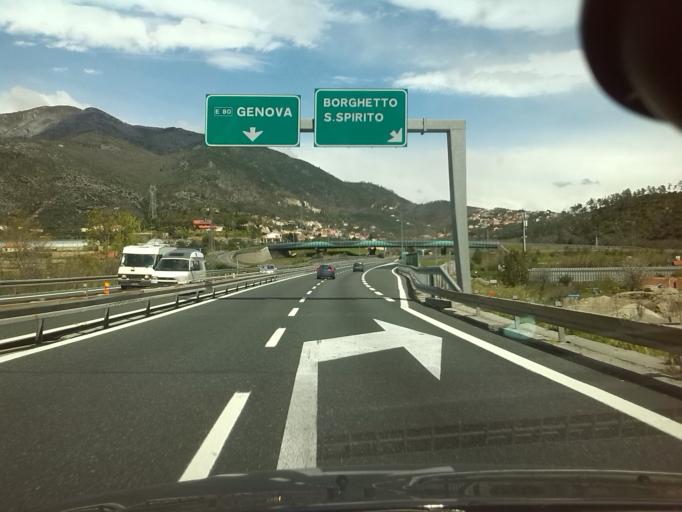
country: IT
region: Liguria
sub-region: Provincia di Savona
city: Boissano
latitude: 44.1207
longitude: 8.2252
